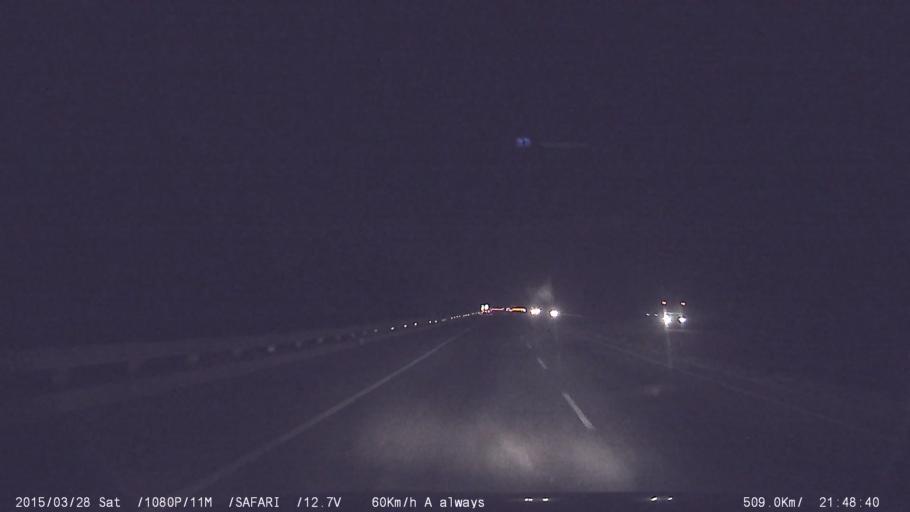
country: IN
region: Karnataka
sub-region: Bangalore Urban
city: Bangalore
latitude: 12.8672
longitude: 77.5068
